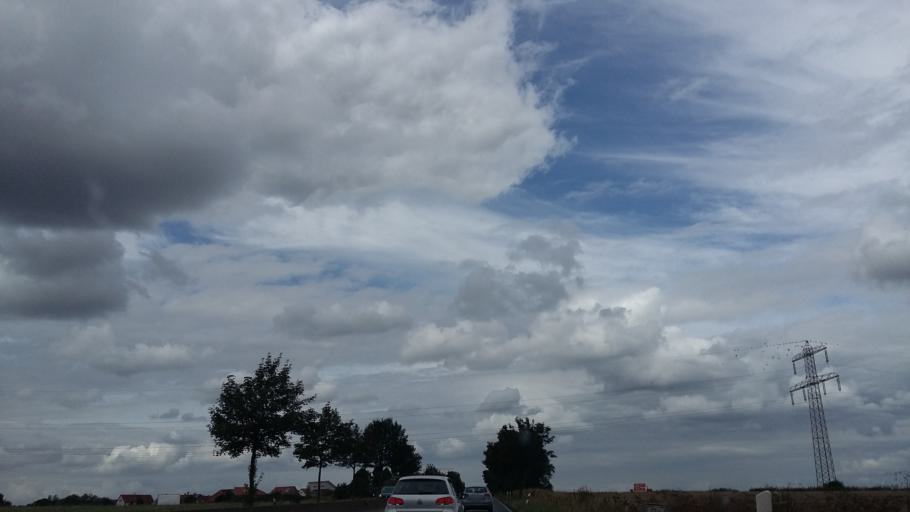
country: DE
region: Lower Saxony
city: Sarstedt
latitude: 52.2801
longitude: 9.8431
